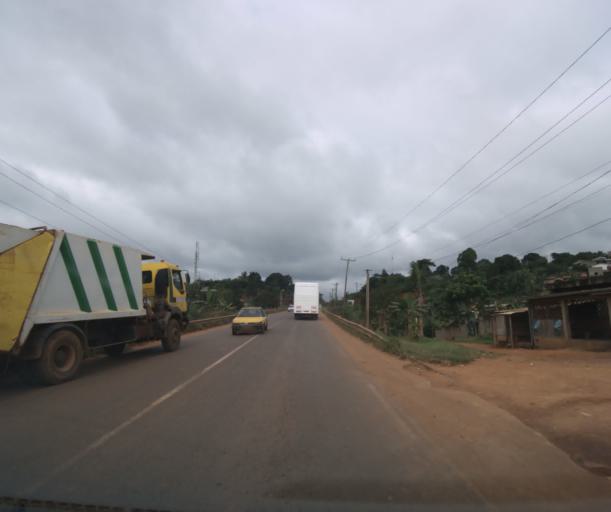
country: CM
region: Centre
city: Yaounde
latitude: 3.7967
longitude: 11.4987
